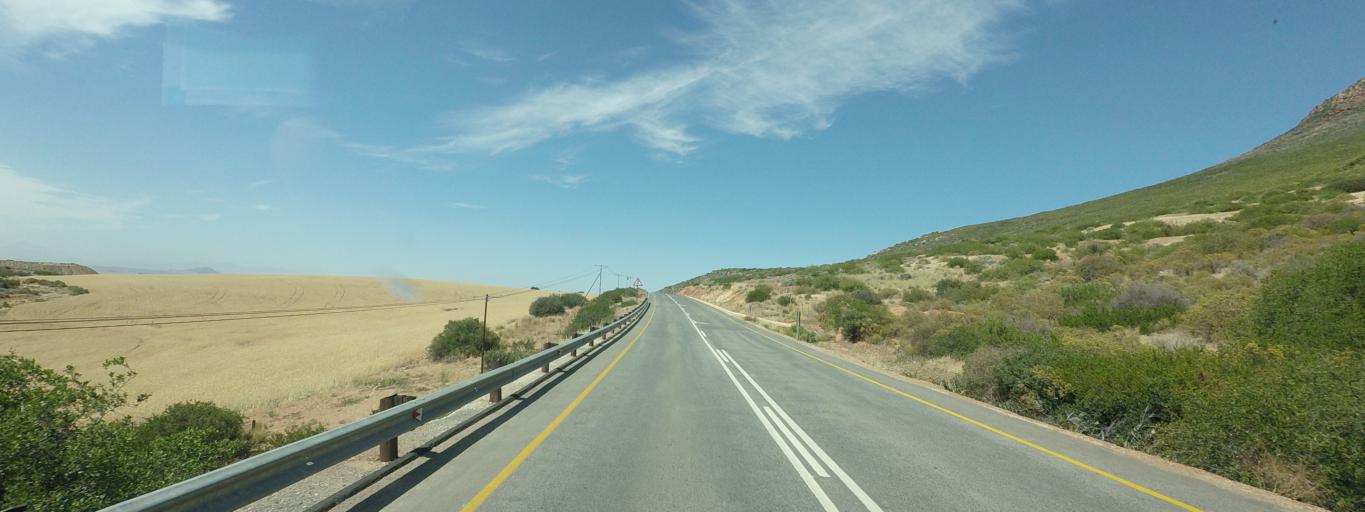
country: ZA
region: Western Cape
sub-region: West Coast District Municipality
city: Piketberg
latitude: -32.9256
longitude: 18.7562
